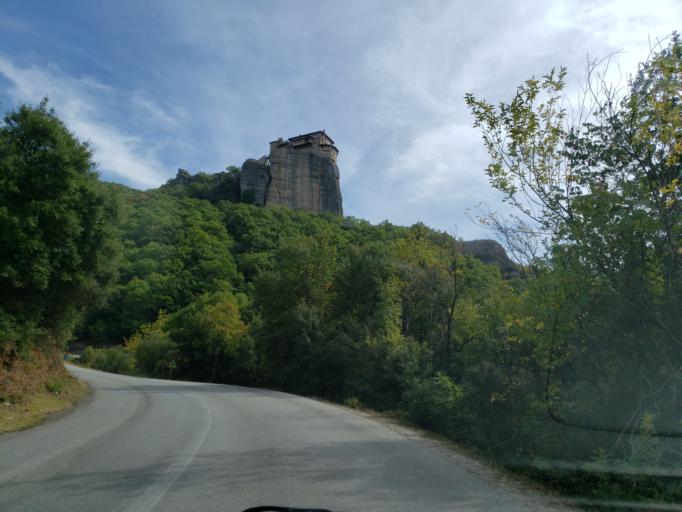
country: GR
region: Thessaly
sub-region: Trikala
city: Kastraki
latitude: 39.7226
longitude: 21.6294
